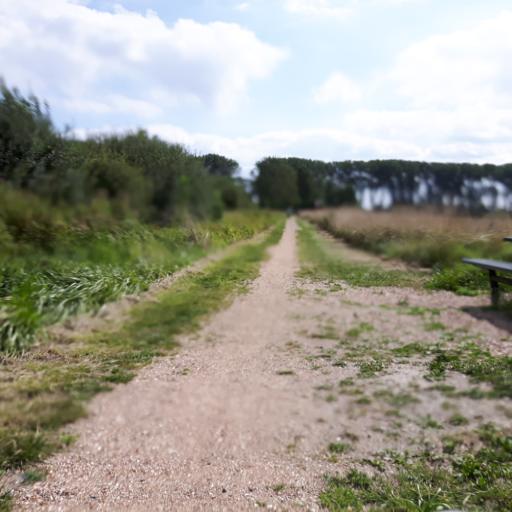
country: NL
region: Zeeland
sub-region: Gemeente Goes
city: Goes
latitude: 51.4444
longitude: 3.8853
